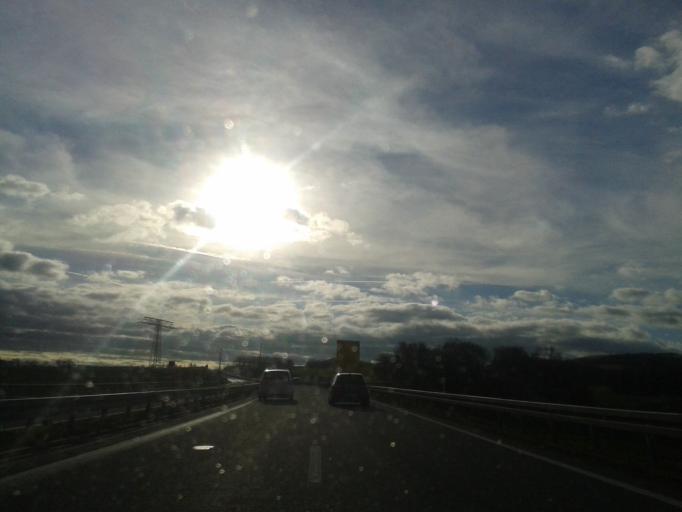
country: DE
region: Saxony
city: Weissenberg
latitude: 51.1565
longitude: 14.6539
